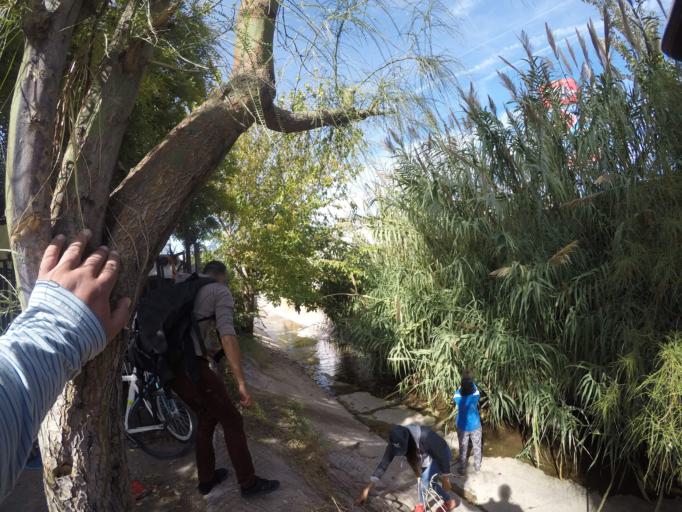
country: MX
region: Chihuahua
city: Ciudad Juarez
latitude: 31.7342
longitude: -106.4501
